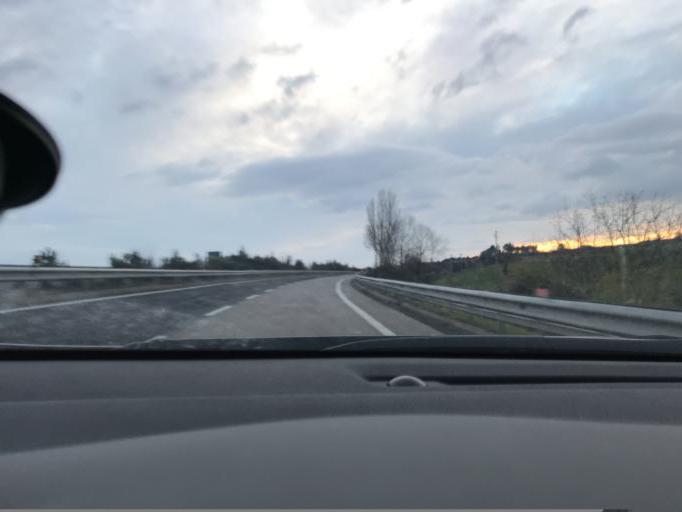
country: IT
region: Umbria
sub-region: Provincia di Perugia
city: Petrignano
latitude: 43.1123
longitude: 12.5061
